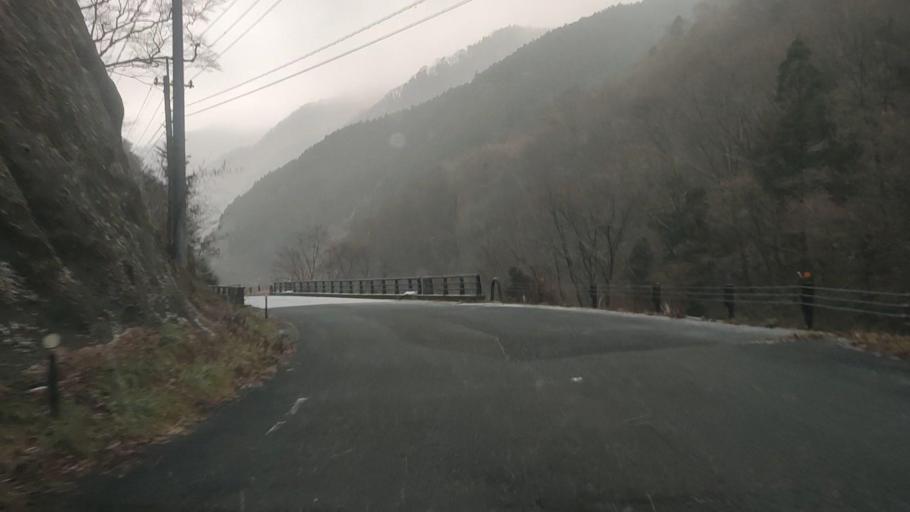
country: JP
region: Kumamoto
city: Matsubase
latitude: 32.5622
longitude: 130.9152
